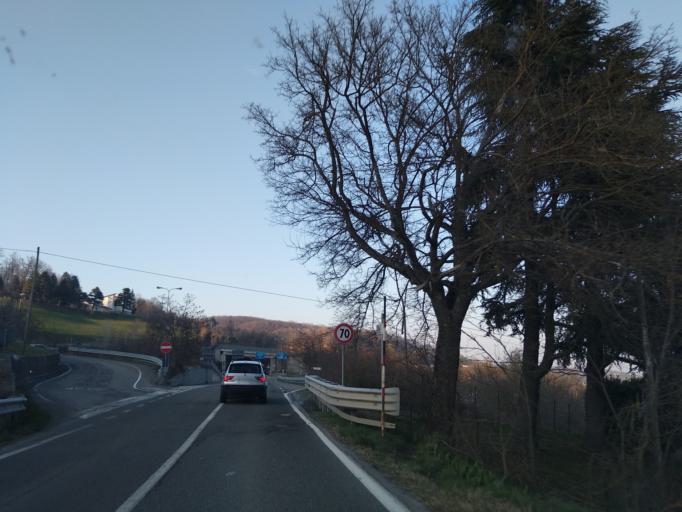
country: IT
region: Emilia-Romagna
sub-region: Provincia di Reggio Emilia
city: Carpineti
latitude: 44.4704
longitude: 10.4897
